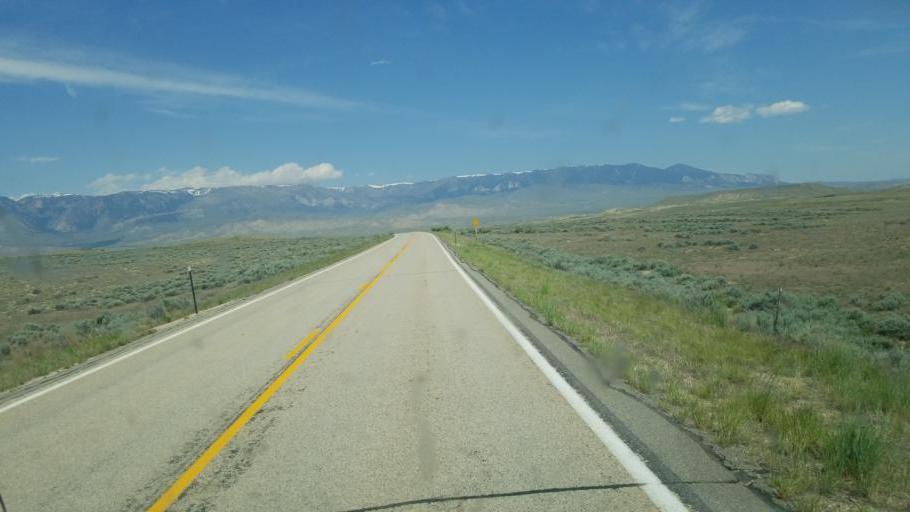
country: US
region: Montana
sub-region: Carbon County
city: Red Lodge
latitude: 44.8978
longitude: -109.0952
